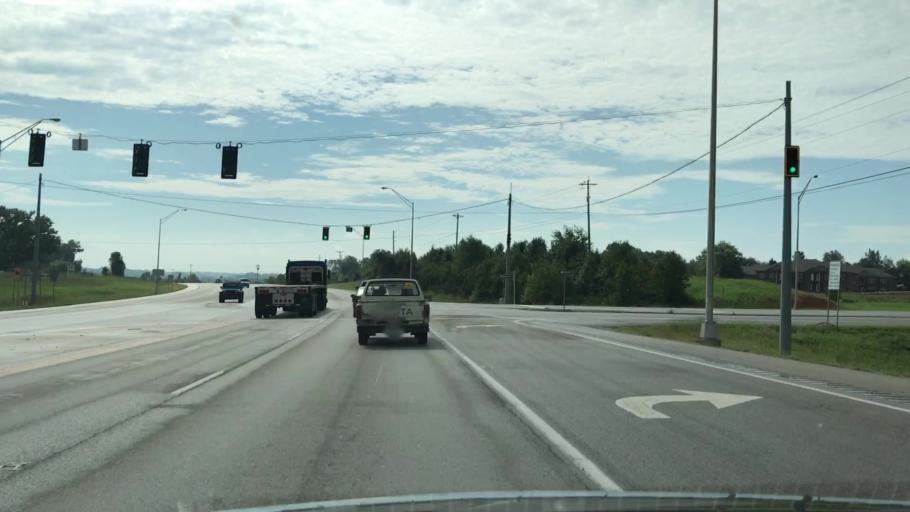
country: US
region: Kentucky
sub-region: Warren County
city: Plano
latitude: 36.9045
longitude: -86.3988
